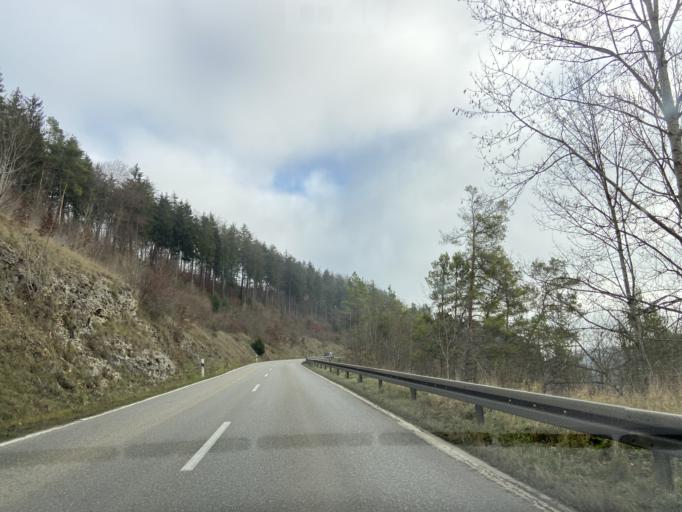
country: DE
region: Baden-Wuerttemberg
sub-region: Tuebingen Region
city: Neufra
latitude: 48.2460
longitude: 9.1882
